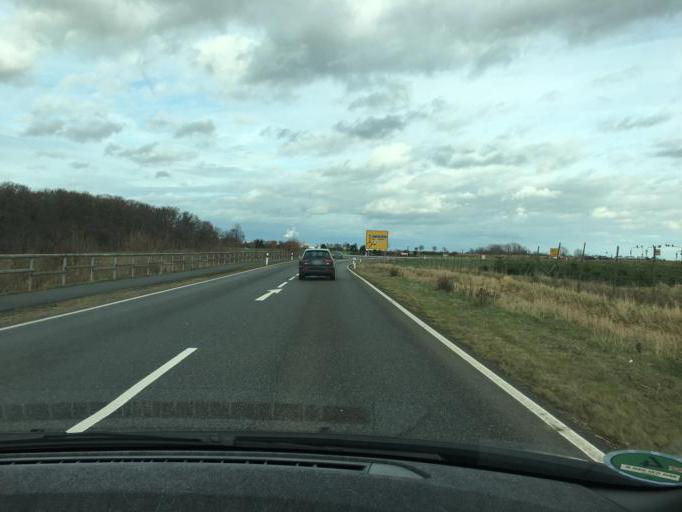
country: DE
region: North Rhine-Westphalia
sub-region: Regierungsbezirk Koln
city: Euskirchen
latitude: 50.6349
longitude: 6.7915
